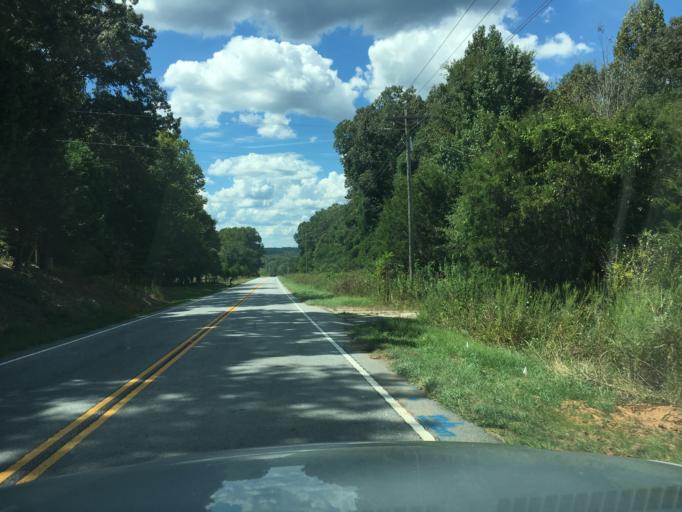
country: US
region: South Carolina
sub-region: Laurens County
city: Laurens
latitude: 34.5230
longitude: -82.1176
